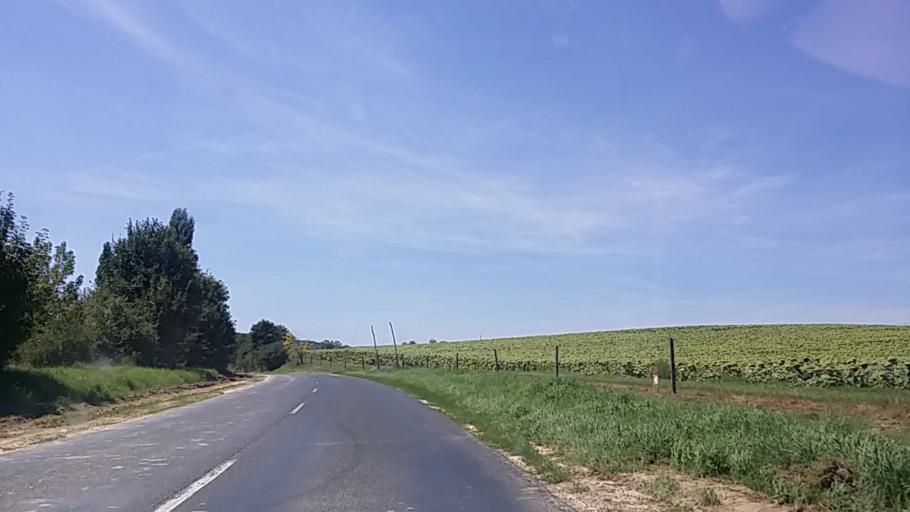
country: HU
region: Somogy
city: Tab
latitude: 46.7150
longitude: 17.9988
